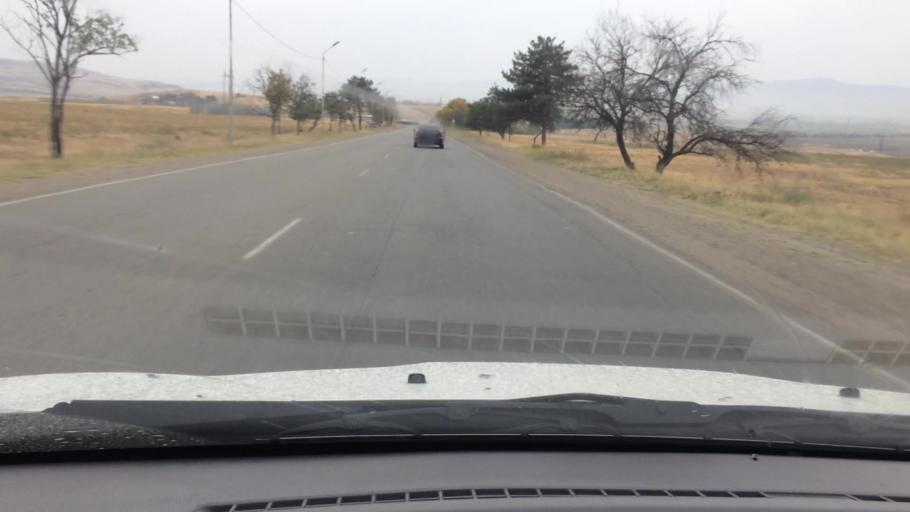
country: GE
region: Kvemo Kartli
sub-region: Marneuli
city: Marneuli
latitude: 41.5149
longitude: 44.7867
